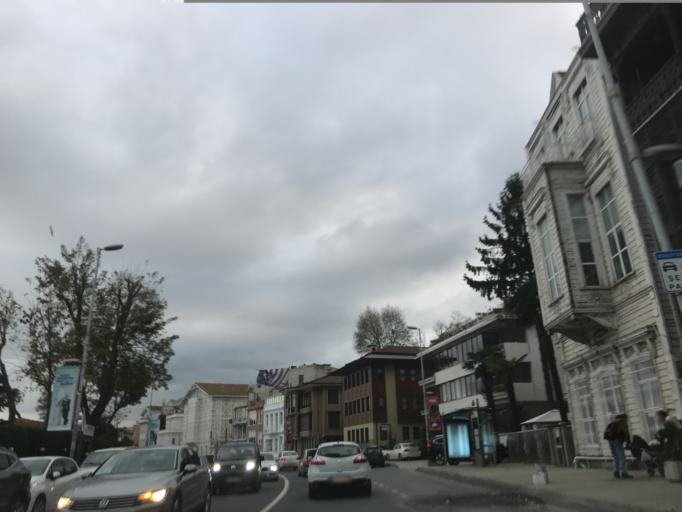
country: TR
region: Istanbul
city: Arikoey
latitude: 41.1637
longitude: 29.0498
